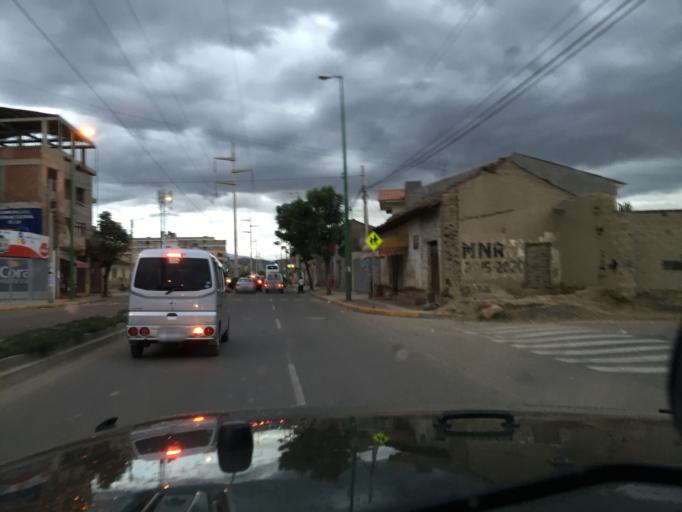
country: BO
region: Cochabamba
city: Cochabamba
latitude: -17.3963
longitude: -66.1835
